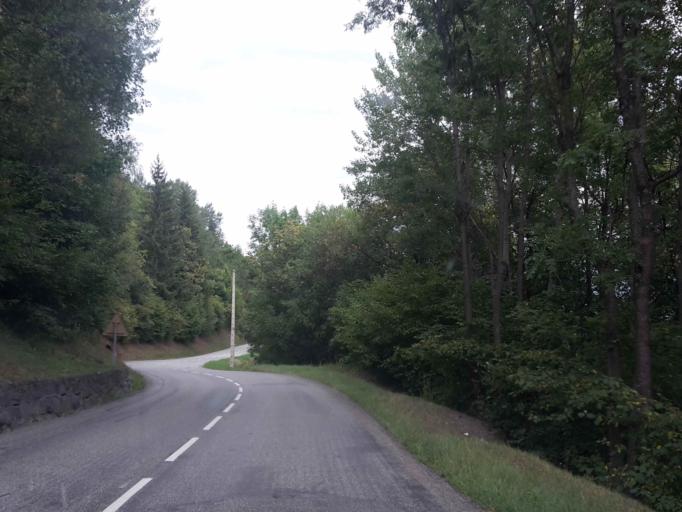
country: FR
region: Rhone-Alpes
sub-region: Departement de la Savoie
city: Saint-Michel-de-Maurienne
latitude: 45.1952
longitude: 6.4687
